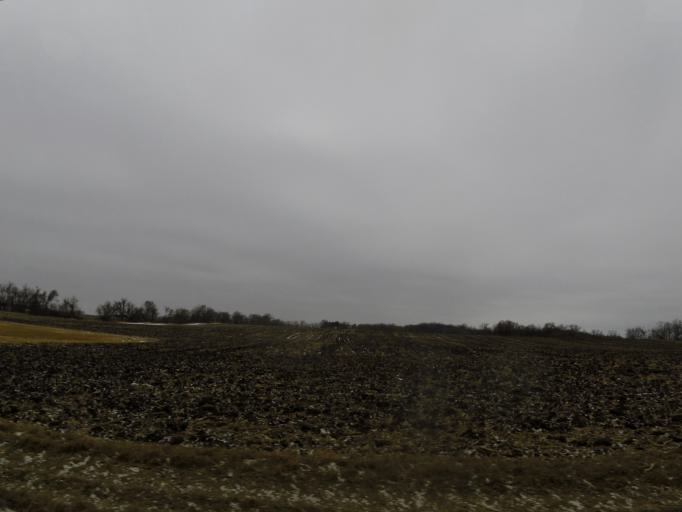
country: US
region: Minnesota
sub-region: Wright County
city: Montrose
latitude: 45.0411
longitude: -93.8585
